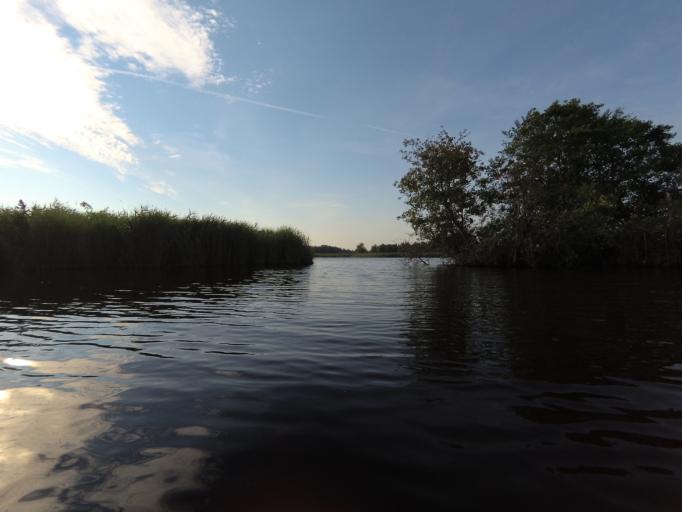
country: NL
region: Overijssel
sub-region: Gemeente Steenwijkerland
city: Sint Jansklooster
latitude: 52.6792
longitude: 6.0611
